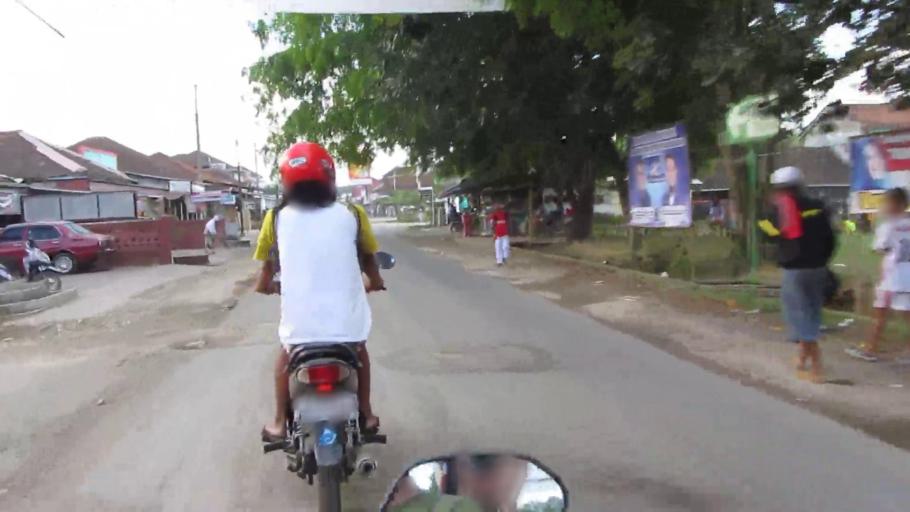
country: ID
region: West Java
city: Cijulang
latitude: -7.7305
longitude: 108.4737
